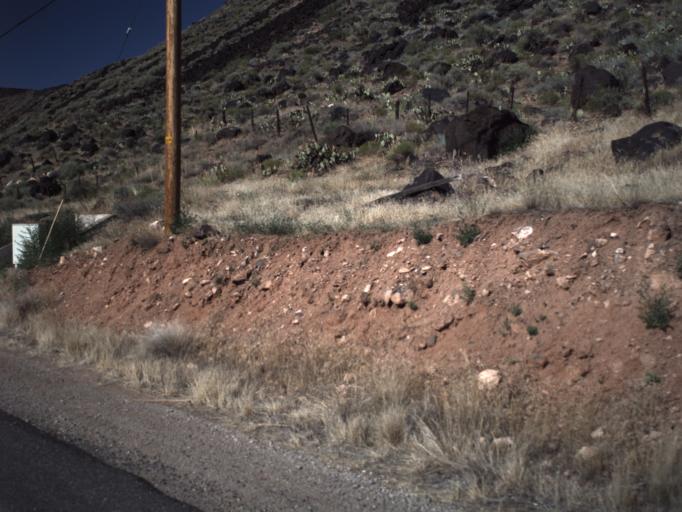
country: US
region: Utah
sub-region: Washington County
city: Toquerville
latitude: 37.2490
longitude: -113.2837
